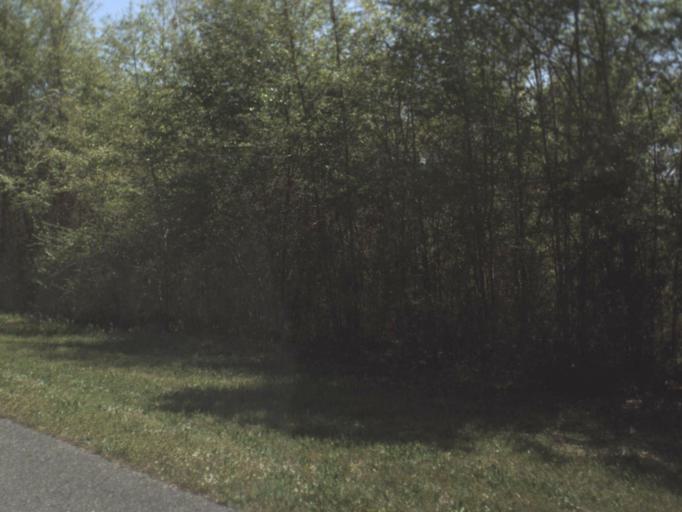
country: US
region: Alabama
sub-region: Escambia County
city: East Brewton
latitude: 30.9511
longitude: -87.0863
